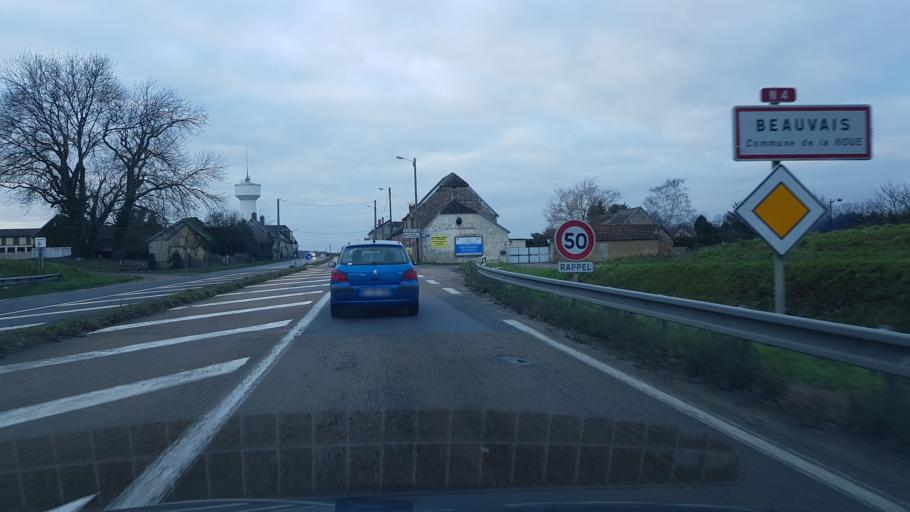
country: FR
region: Champagne-Ardenne
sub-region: Departement de la Marne
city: Esternay
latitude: 48.7316
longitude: 3.6139
